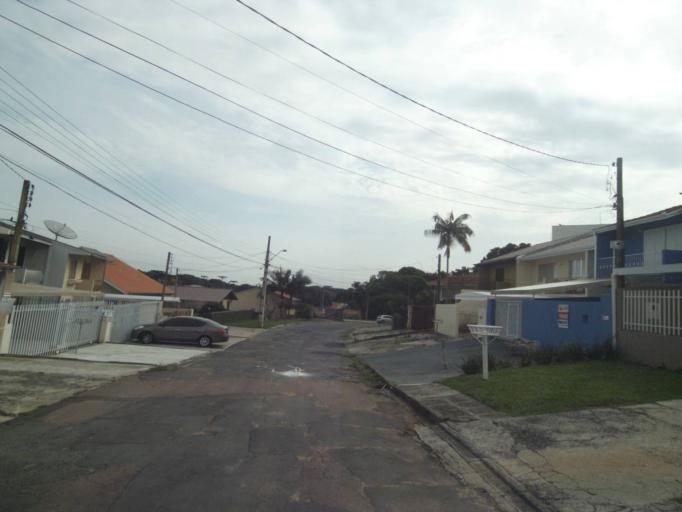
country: BR
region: Parana
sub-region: Curitiba
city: Curitiba
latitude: -25.4111
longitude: -49.2992
